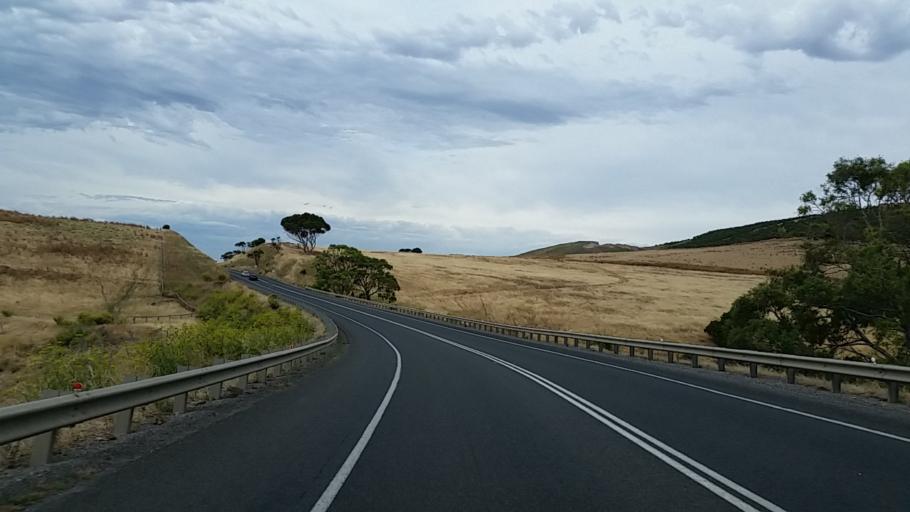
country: AU
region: South Australia
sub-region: Onkaparinga
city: Port Willunga
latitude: -35.3497
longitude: 138.4537
